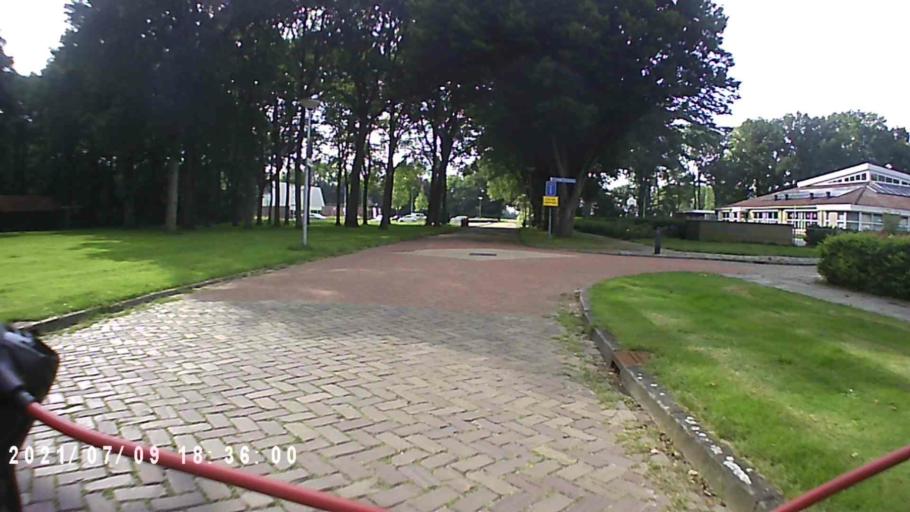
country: NL
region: Groningen
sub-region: Gemeente Pekela
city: Oude Pekela
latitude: 53.0762
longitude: 6.9584
